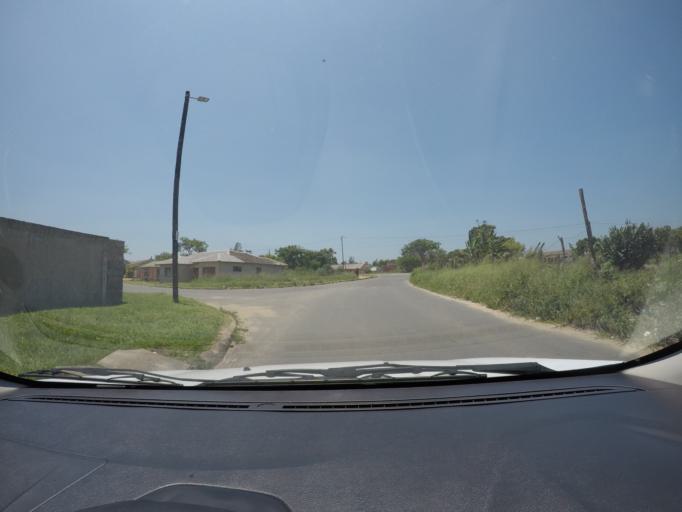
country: ZA
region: KwaZulu-Natal
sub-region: uThungulu District Municipality
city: eSikhawini
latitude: -28.8783
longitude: 31.9101
